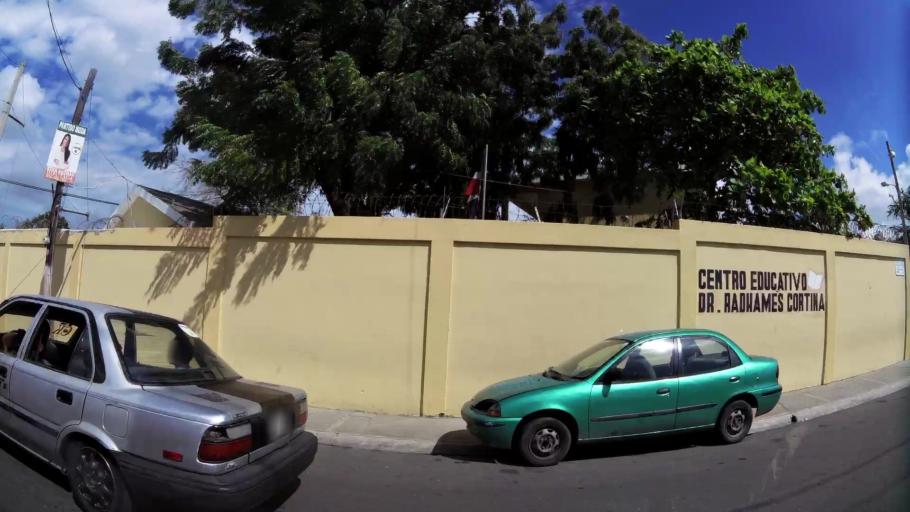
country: DO
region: Santiago
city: Santiago de los Caballeros
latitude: 19.4724
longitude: -70.7005
